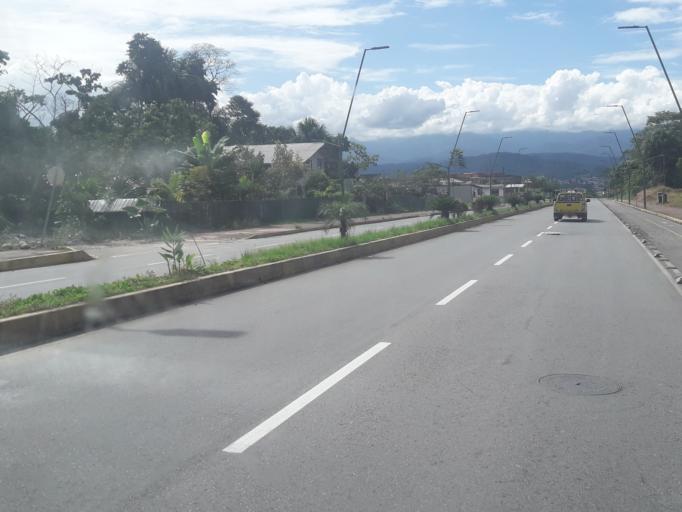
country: EC
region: Napo
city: Tena
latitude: -1.0143
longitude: -77.8081
